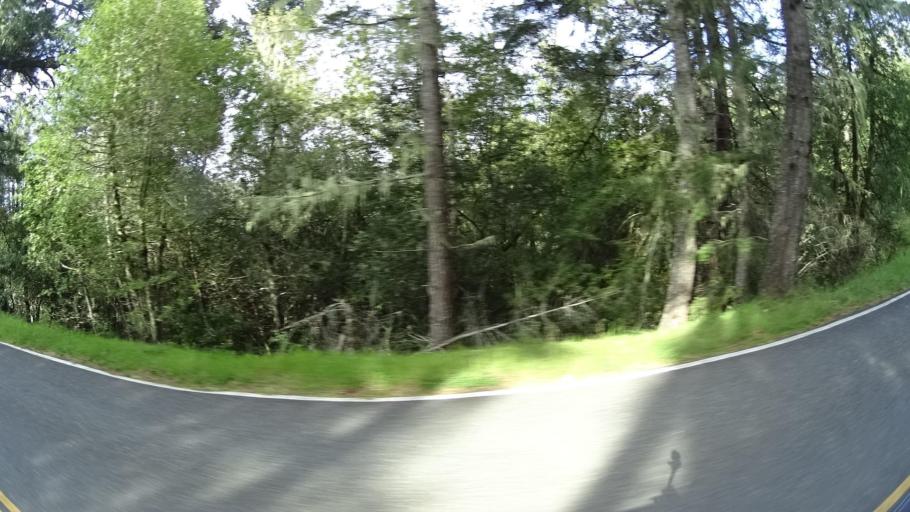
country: US
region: California
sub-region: Humboldt County
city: Blue Lake
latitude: 40.7414
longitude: -123.9600
